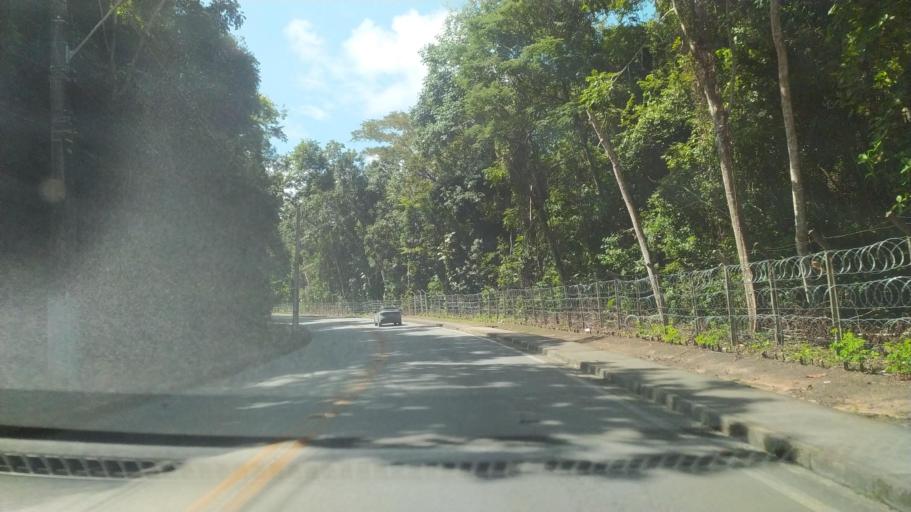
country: BR
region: Alagoas
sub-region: Maceio
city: Maceio
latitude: -9.5972
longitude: -35.7378
